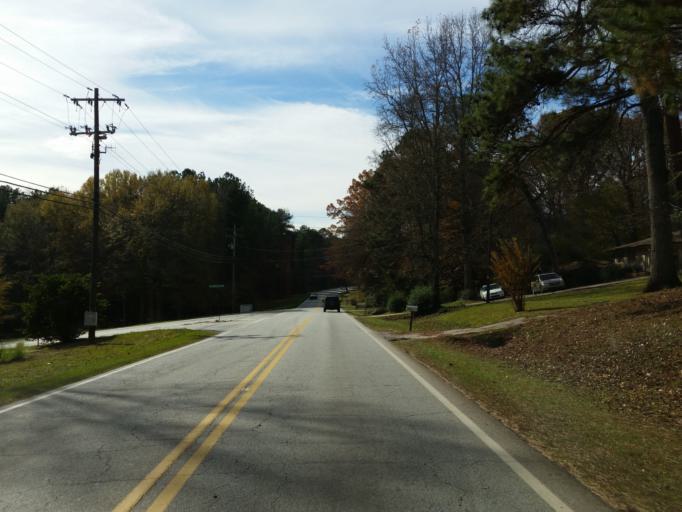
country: US
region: Georgia
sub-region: Douglas County
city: Lithia Springs
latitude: 33.7504
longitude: -84.6572
